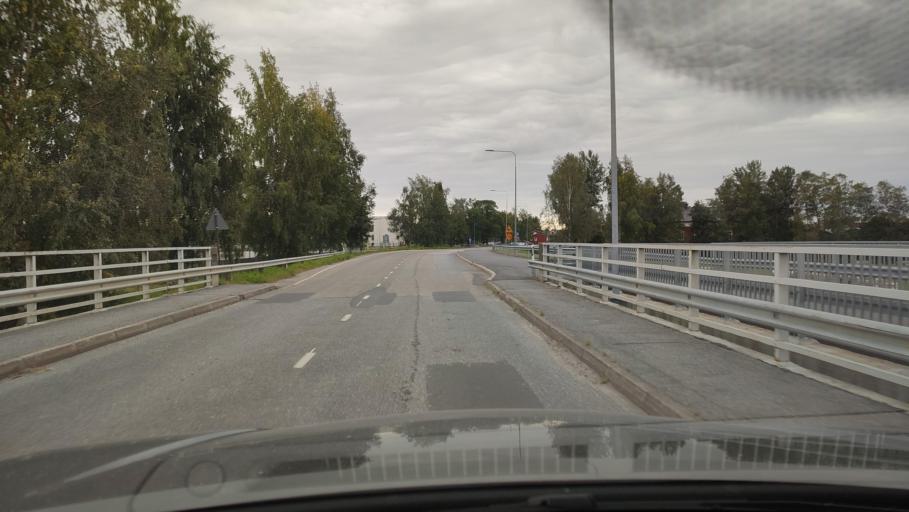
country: FI
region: Ostrobothnia
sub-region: Sydosterbotten
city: Kristinestad
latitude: 62.2560
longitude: 21.5263
